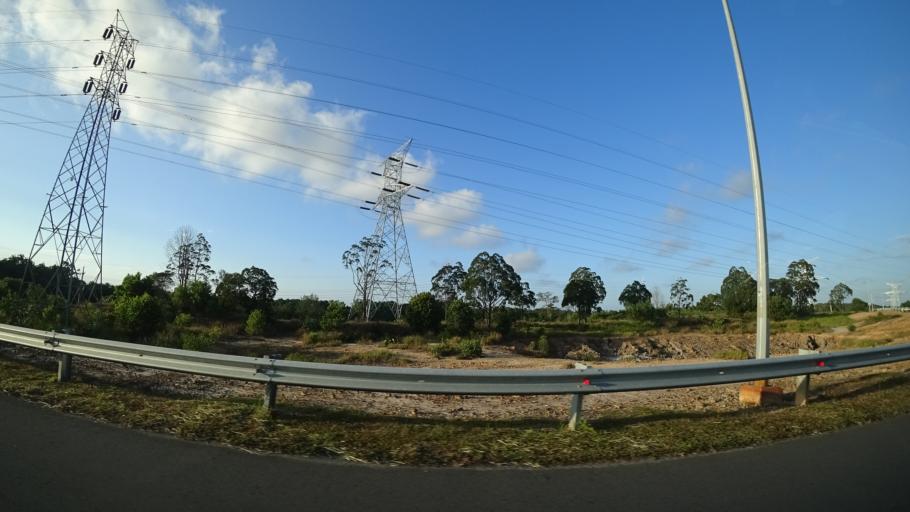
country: BN
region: Tutong
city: Tutong
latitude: 4.7342
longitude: 114.5794
